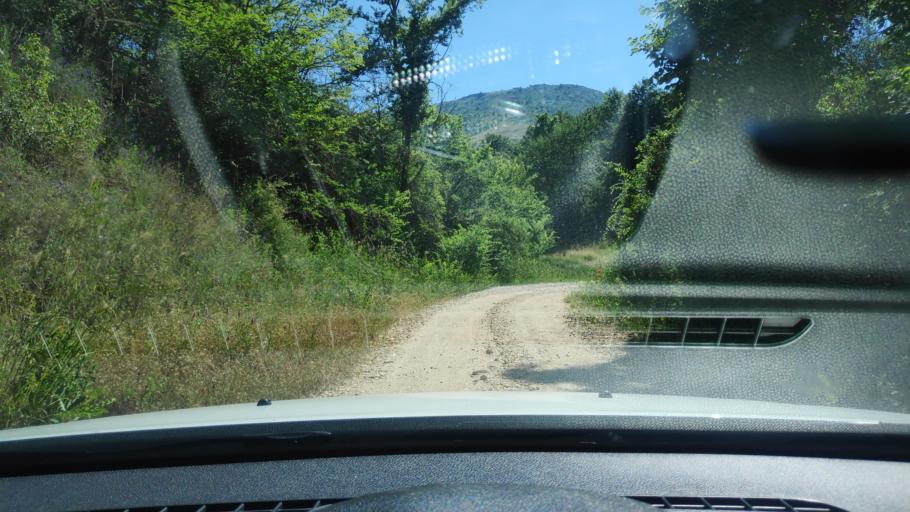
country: MK
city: Klechovce
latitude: 42.0728
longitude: 21.8982
